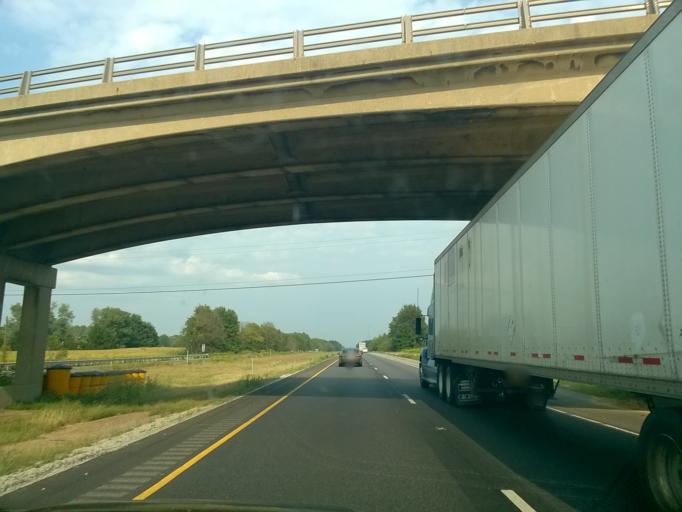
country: US
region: Indiana
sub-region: Clay County
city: Brazil
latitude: 39.4635
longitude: -87.0705
